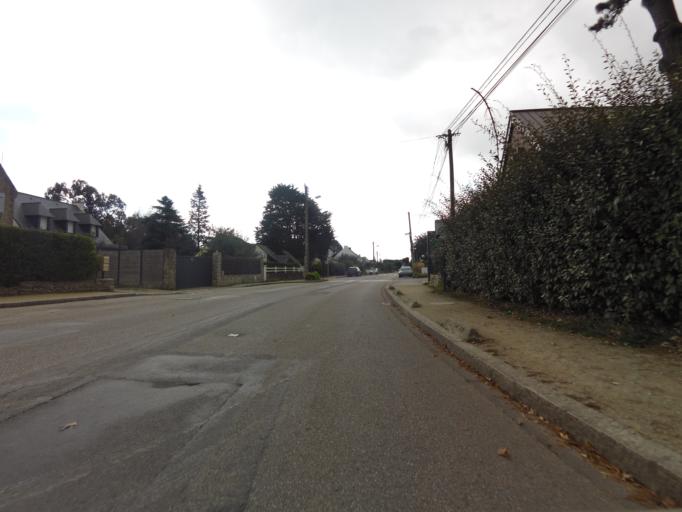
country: FR
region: Brittany
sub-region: Departement du Morbihan
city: Carnac
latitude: 47.5844
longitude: -3.0751
